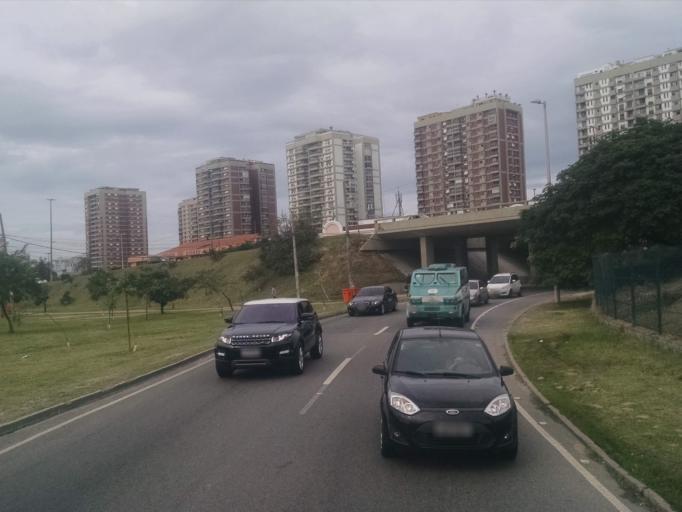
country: BR
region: Rio de Janeiro
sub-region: Rio De Janeiro
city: Rio de Janeiro
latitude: -22.9997
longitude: -43.3632
